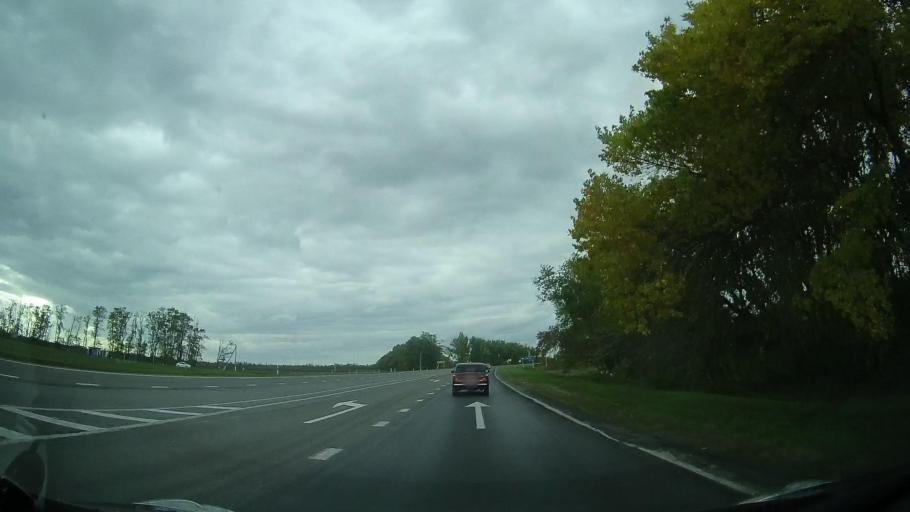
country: RU
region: Rostov
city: Yegorlykskaya
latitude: 46.5371
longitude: 40.7829
